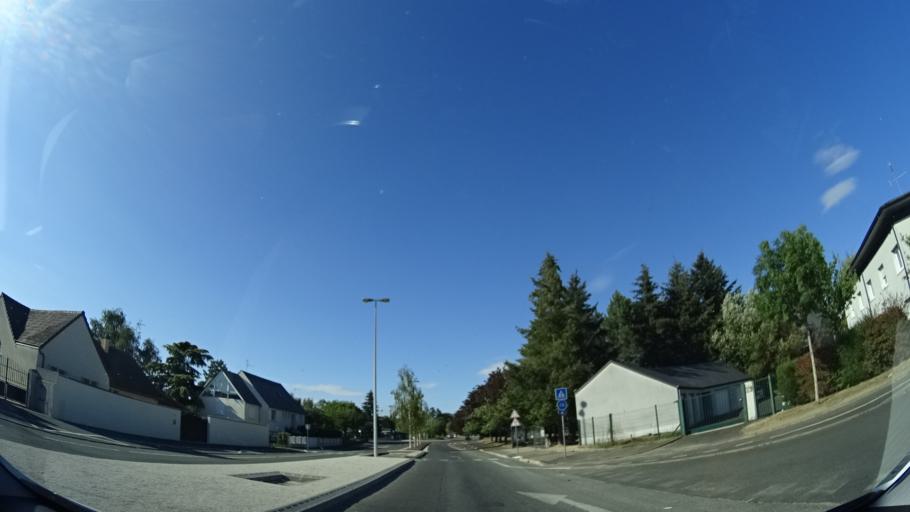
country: FR
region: Centre
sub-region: Departement du Loiret
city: Saint-Jean-de-Braye
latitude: 47.9135
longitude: 1.9782
